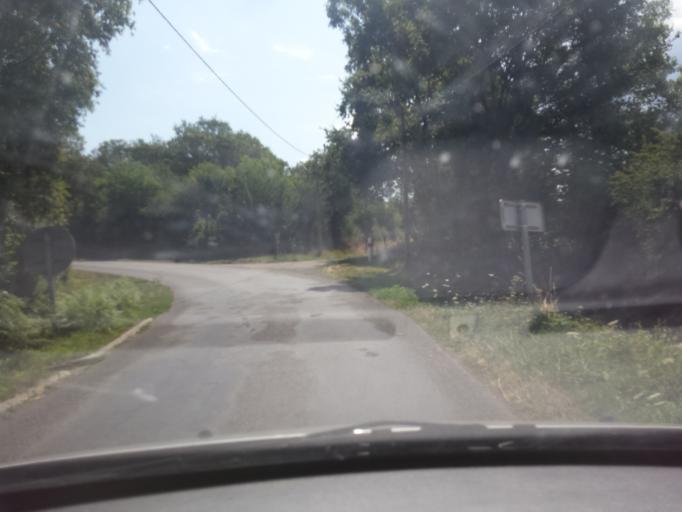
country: FR
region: Poitou-Charentes
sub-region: Departement de la Vienne
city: Availles-Limouzine
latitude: 46.1077
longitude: 0.6853
